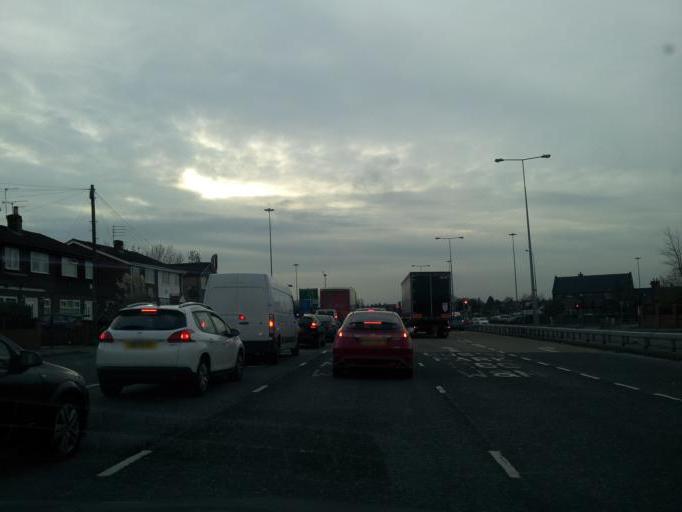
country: GB
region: England
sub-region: Manchester
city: Failsworth
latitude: 53.5287
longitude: -2.1576
